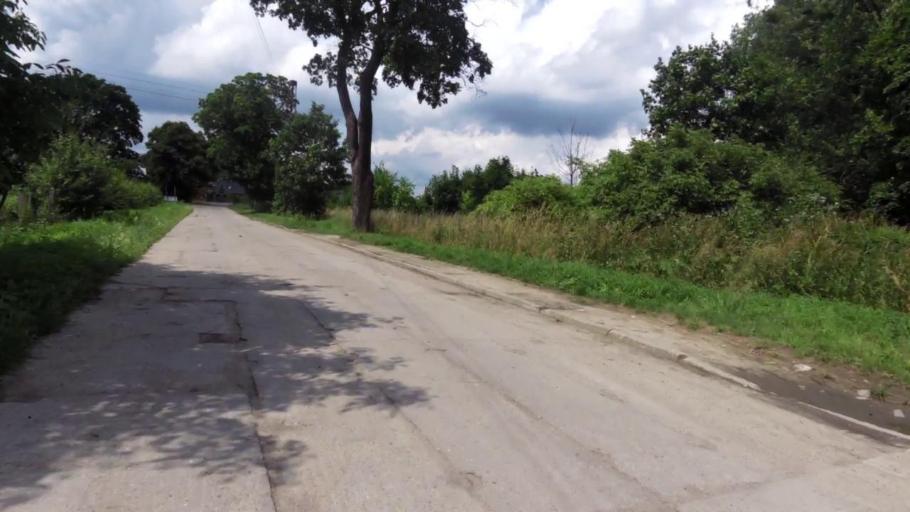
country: PL
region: West Pomeranian Voivodeship
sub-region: Powiat mysliborski
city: Nowogrodek Pomorski
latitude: 52.9879
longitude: 15.0627
